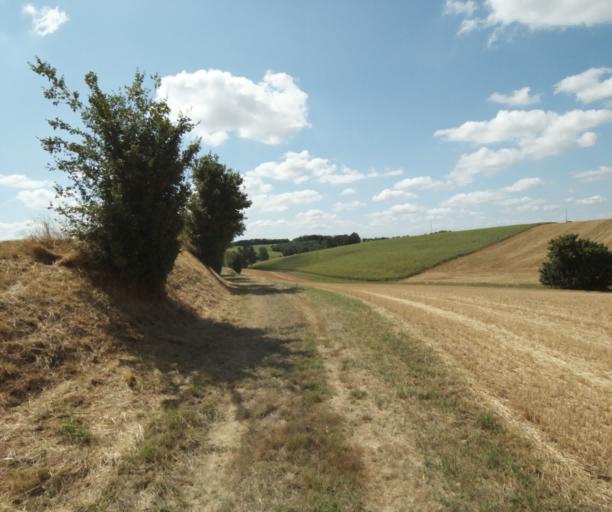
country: FR
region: Midi-Pyrenees
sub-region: Departement de la Haute-Garonne
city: Auriac-sur-Vendinelle
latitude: 43.4619
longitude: 1.7946
